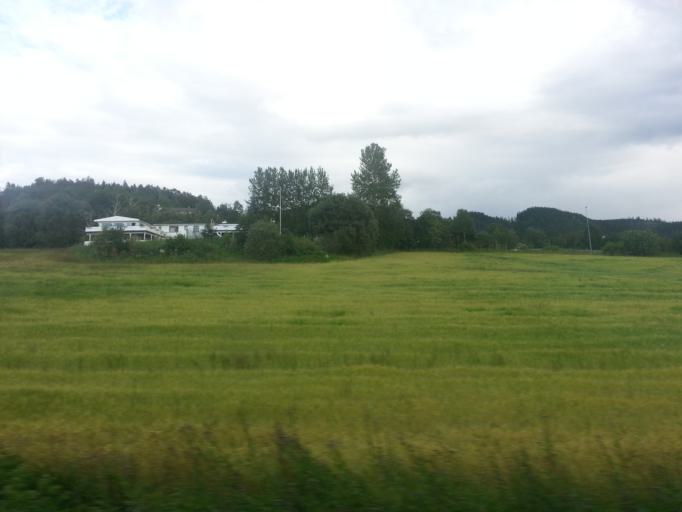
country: NO
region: Sor-Trondelag
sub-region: Malvik
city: Malvik
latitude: 63.4364
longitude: 10.5800
